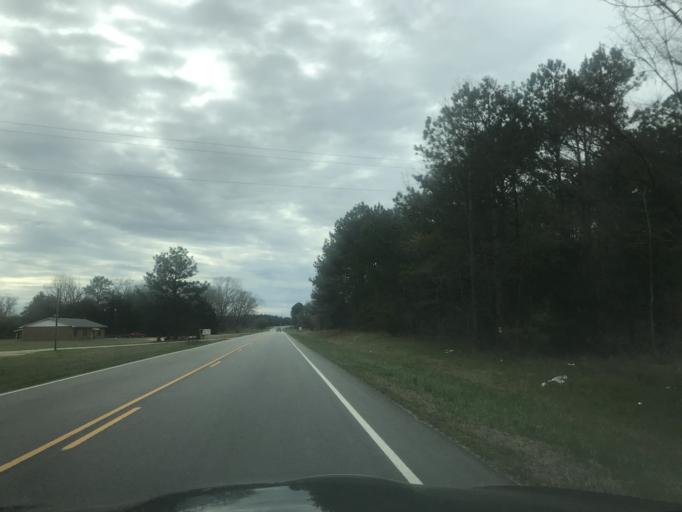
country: US
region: North Carolina
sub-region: Franklin County
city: Louisburg
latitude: 36.0875
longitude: -78.3747
